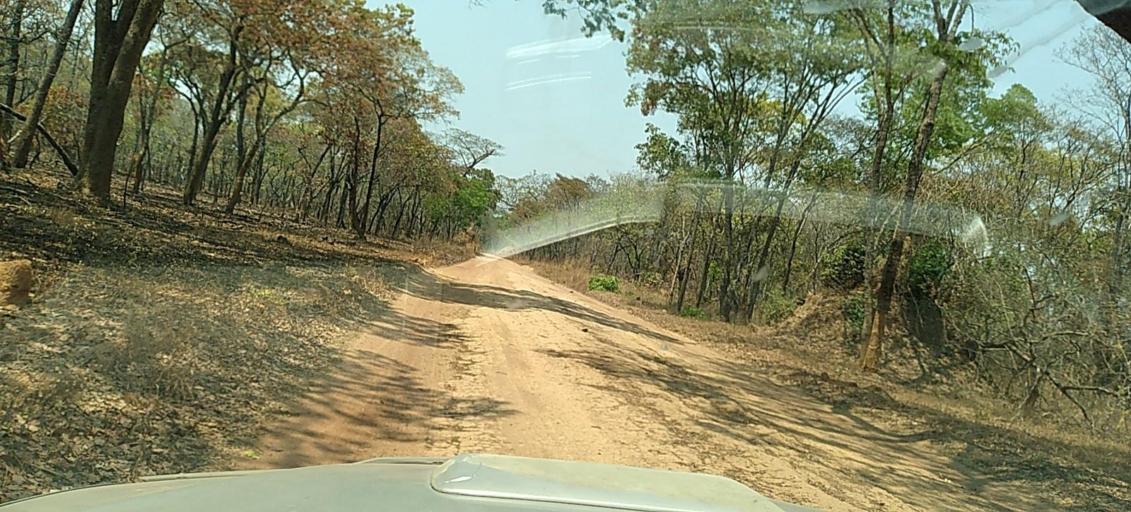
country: ZM
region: North-Western
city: Kasempa
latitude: -13.6092
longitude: 26.1913
